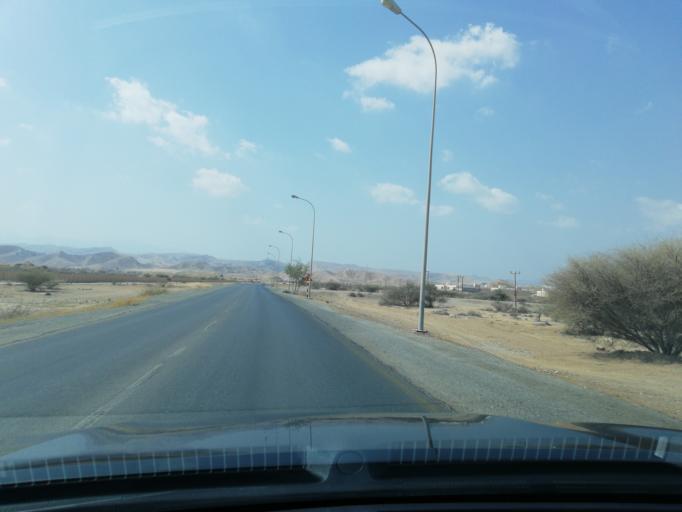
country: OM
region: Muhafazat Masqat
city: As Sib al Jadidah
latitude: 23.5851
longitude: 58.2135
